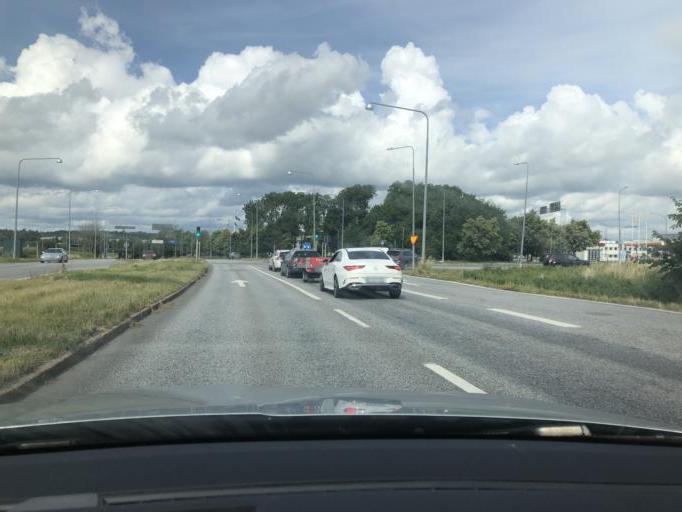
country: SE
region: Uppsala
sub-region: Uppsala Kommun
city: Saevja
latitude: 59.8456
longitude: 17.6777
